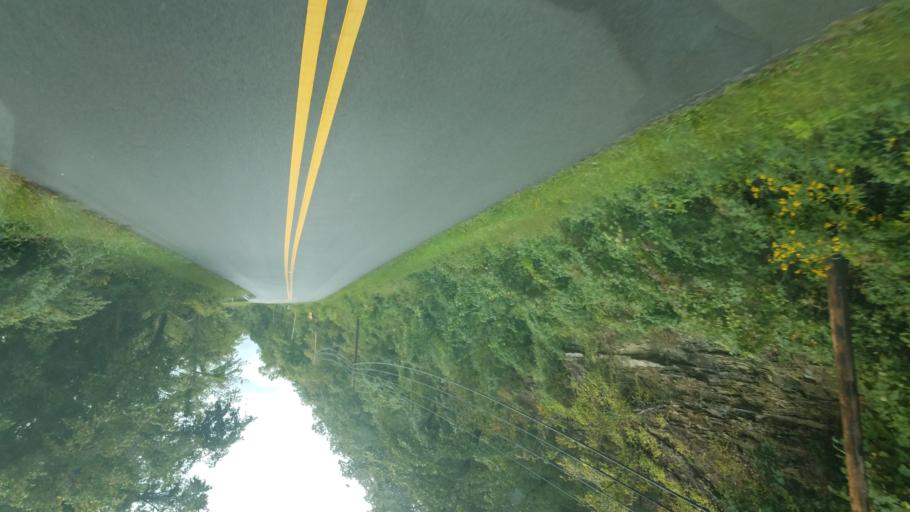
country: US
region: Ohio
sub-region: Scioto County
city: Franklin Furnace
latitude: 38.6493
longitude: -82.8499
